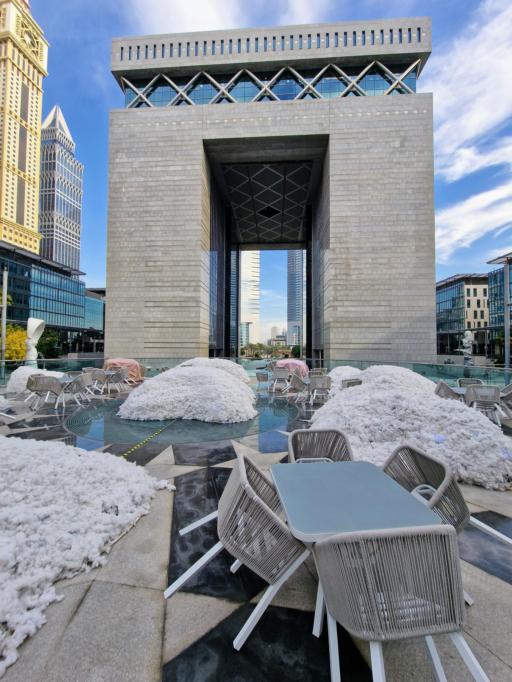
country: AE
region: Ash Shariqah
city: Sharjah
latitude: 25.2138
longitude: 55.2807
